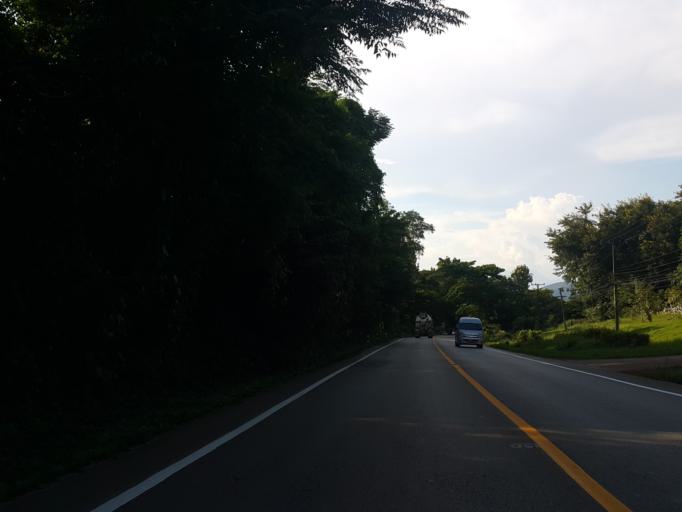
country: TH
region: Chiang Mai
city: Mae Taeng
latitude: 19.0949
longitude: 99.0830
